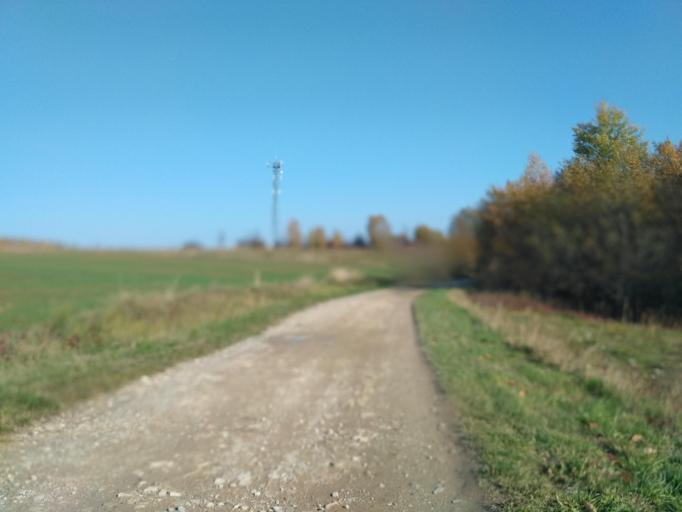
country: PL
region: Subcarpathian Voivodeship
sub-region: Powiat rzeszowski
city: Blazowa
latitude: 49.8722
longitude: 22.0889
